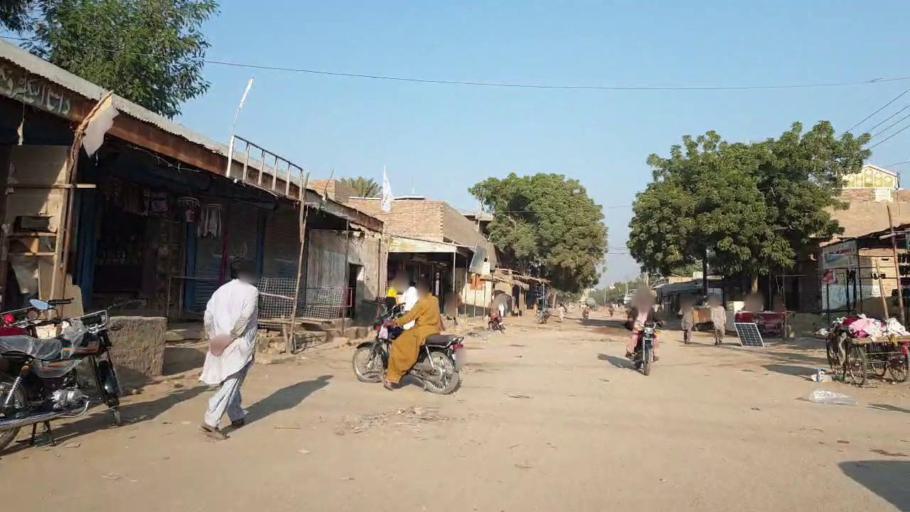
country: PK
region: Sindh
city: Kotri
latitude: 25.3575
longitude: 68.2559
